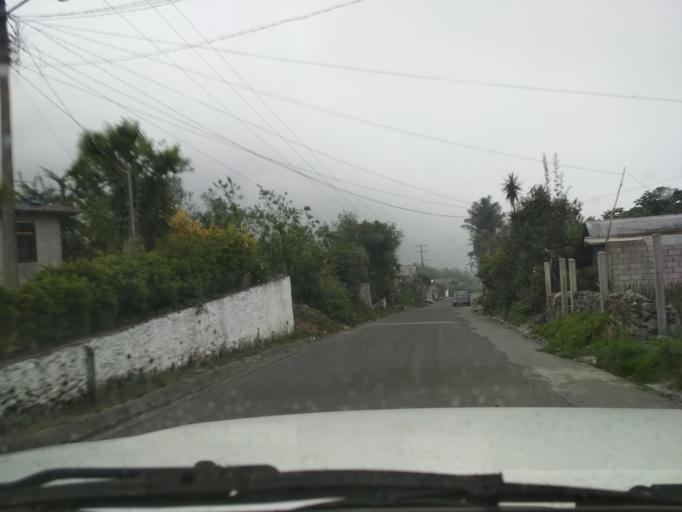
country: MX
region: Veracruz
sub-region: Mariano Escobedo
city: San Isidro el Berro
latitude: 18.9542
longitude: -97.1793
